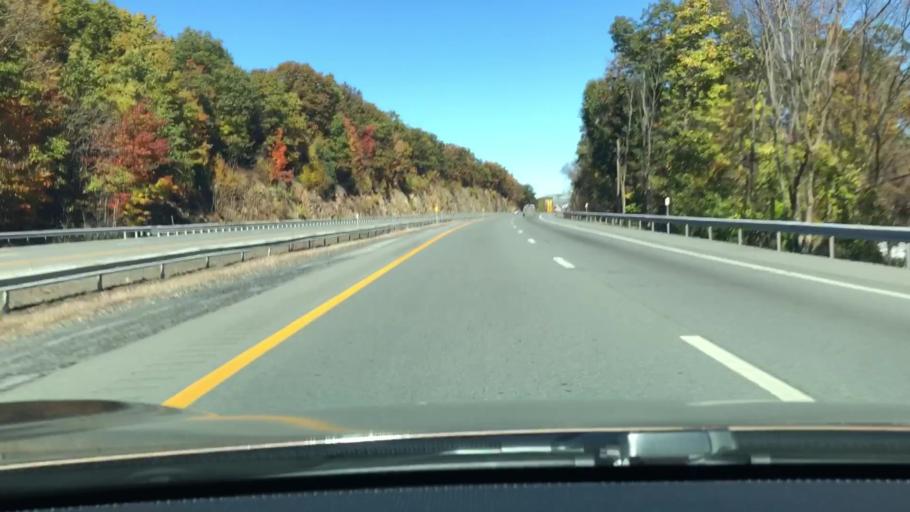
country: US
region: New York
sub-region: Orange County
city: Highland Mills
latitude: 41.3445
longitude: -74.1170
